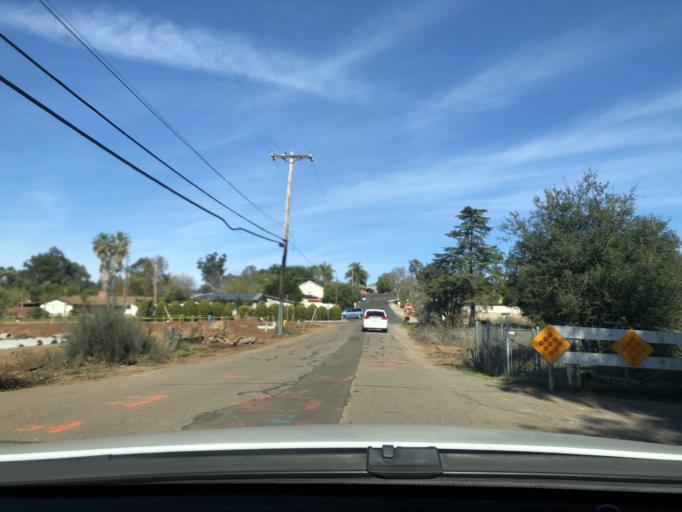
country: US
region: California
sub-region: San Diego County
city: Escondido
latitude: 33.0878
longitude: -117.0811
